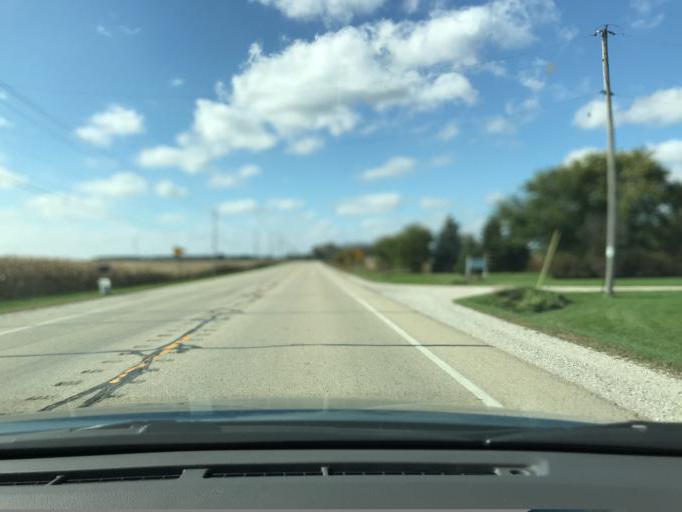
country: US
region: Wisconsin
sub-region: Kenosha County
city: Somers
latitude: 42.6249
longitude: -87.9884
